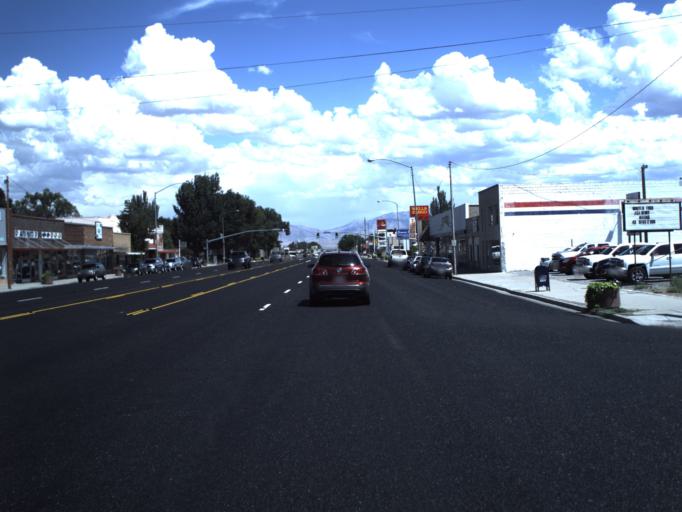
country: US
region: Utah
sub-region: Millard County
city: Delta
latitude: 39.3524
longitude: -112.5816
